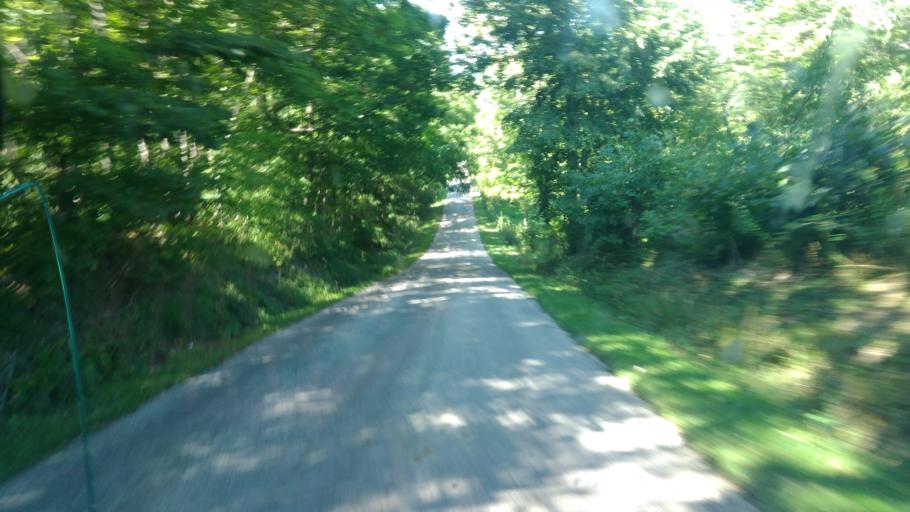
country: US
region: Ohio
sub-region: Ashland County
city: Ashland
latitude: 40.9313
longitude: -82.2626
